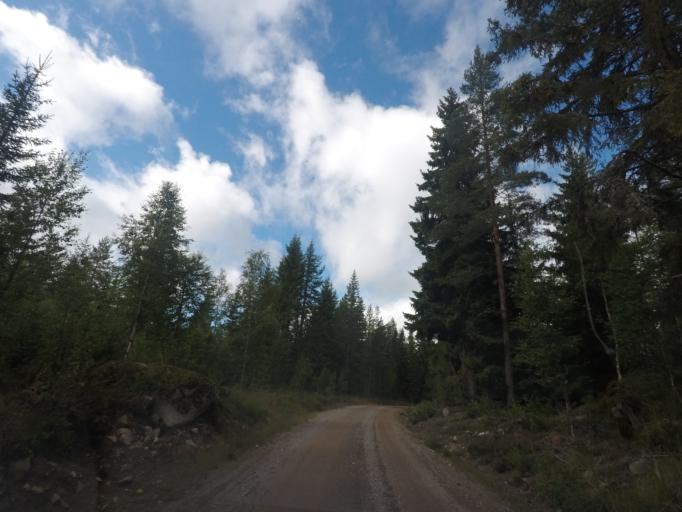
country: SE
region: Vaermland
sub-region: Filipstads Kommun
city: Lesjofors
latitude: 60.0897
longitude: 14.4050
